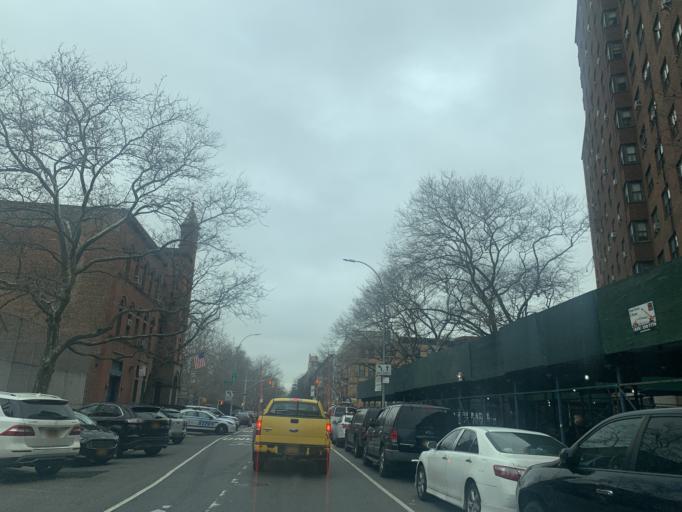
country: US
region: New York
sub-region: Kings County
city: Brooklyn
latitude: 40.6897
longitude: -73.9601
